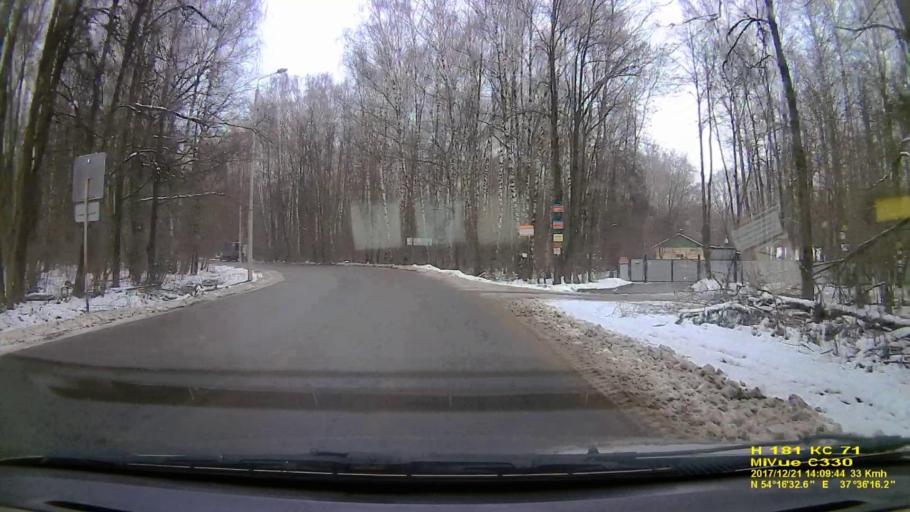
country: RU
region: Tula
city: Gorelki
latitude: 54.2759
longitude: 37.6047
